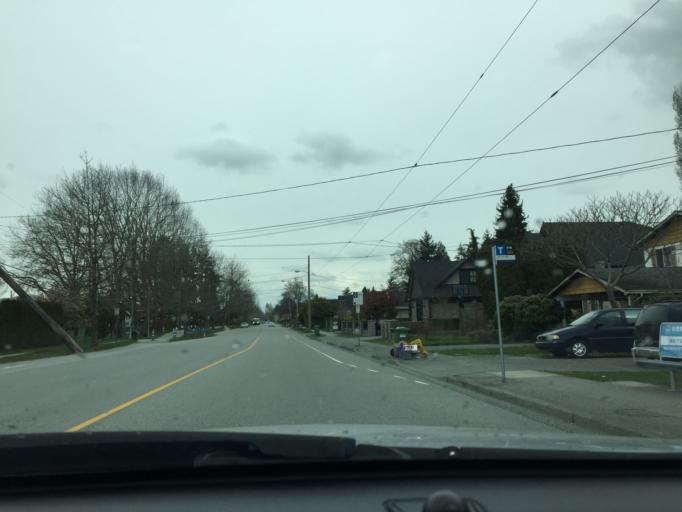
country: CA
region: British Columbia
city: Richmond
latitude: 49.1411
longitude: -123.1252
